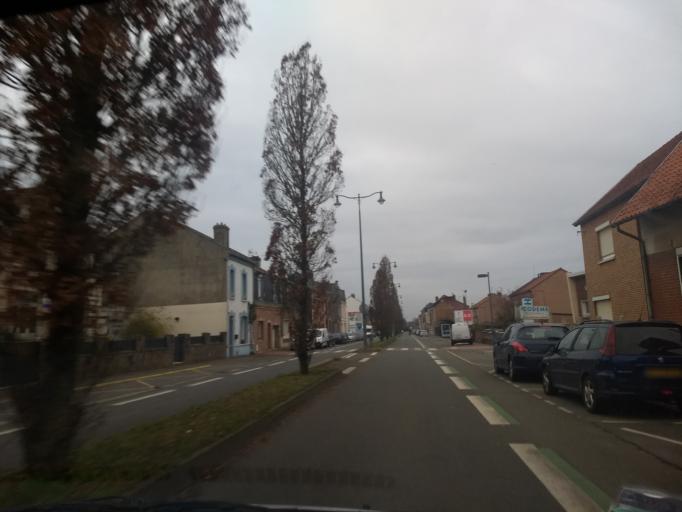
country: FR
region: Nord-Pas-de-Calais
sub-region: Departement du Pas-de-Calais
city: Saint-Laurent-Blangy
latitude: 50.2835
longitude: 2.8005
